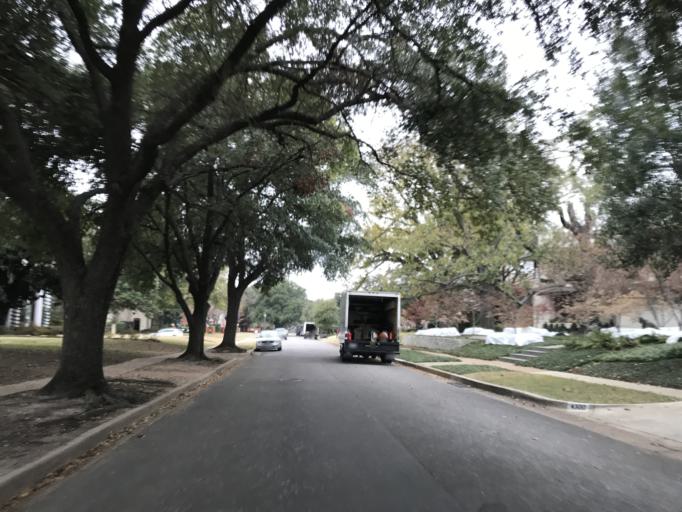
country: US
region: Texas
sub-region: Dallas County
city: Highland Park
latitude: 32.8248
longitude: -96.8085
